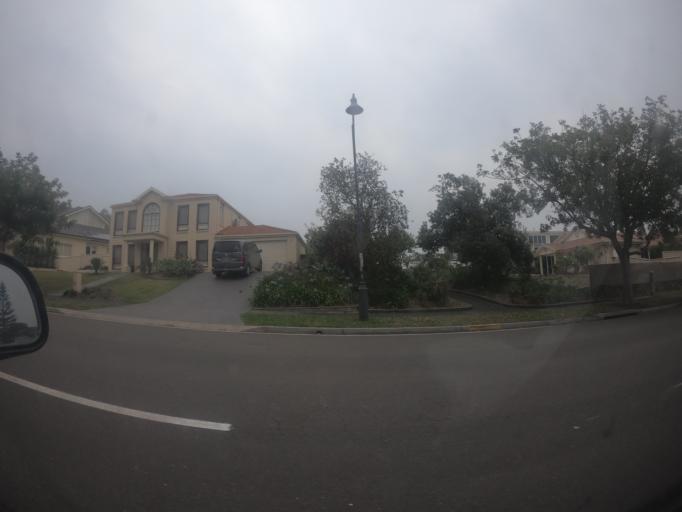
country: AU
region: New South Wales
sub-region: Shellharbour
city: Flinders
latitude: -34.5915
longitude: 150.8578
